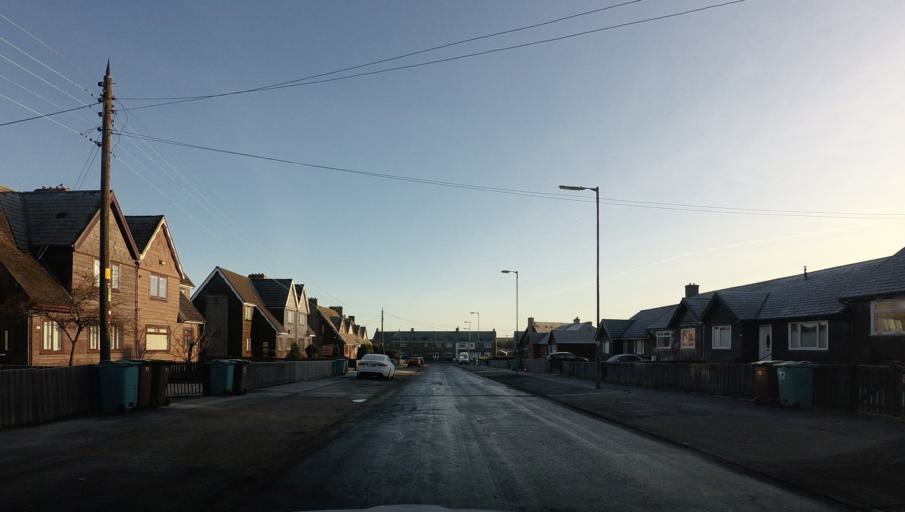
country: GB
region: Scotland
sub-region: North Lanarkshire
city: Shotts
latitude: 55.8222
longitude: -3.7998
